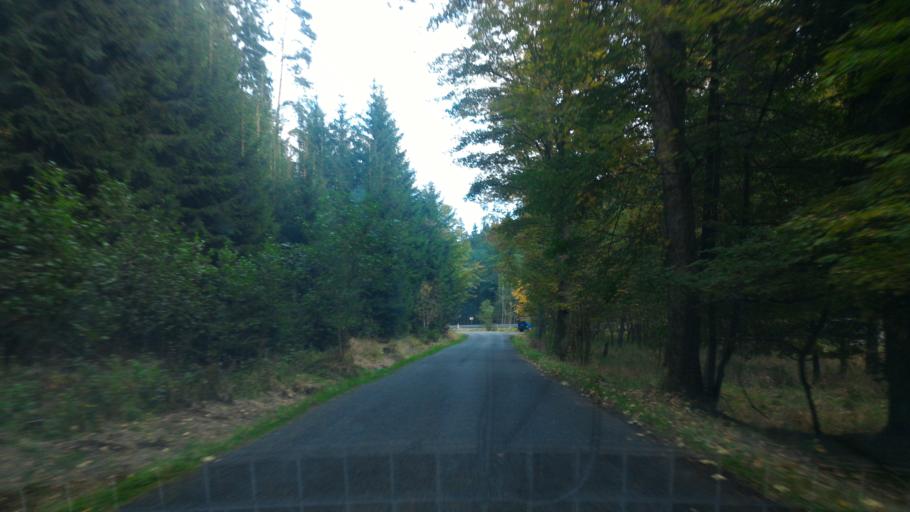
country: CZ
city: Kamenicky Senov
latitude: 50.8108
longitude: 14.4656
